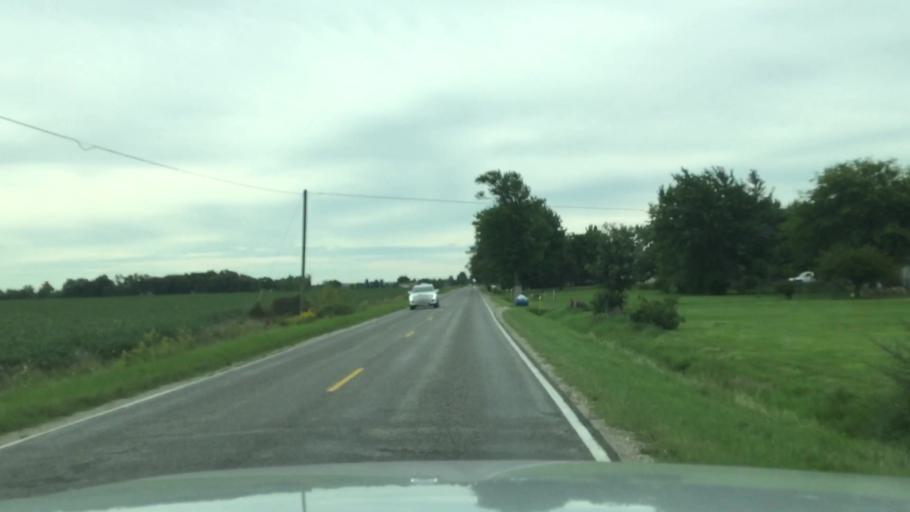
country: US
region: Michigan
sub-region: Shiawassee County
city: Durand
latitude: 43.0472
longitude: -83.9874
